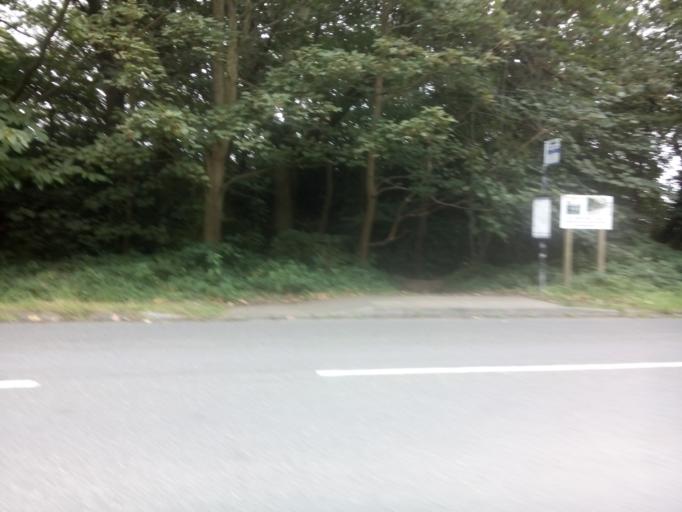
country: GB
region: England
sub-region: Norfolk
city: Briston
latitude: 52.9119
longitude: 1.1132
